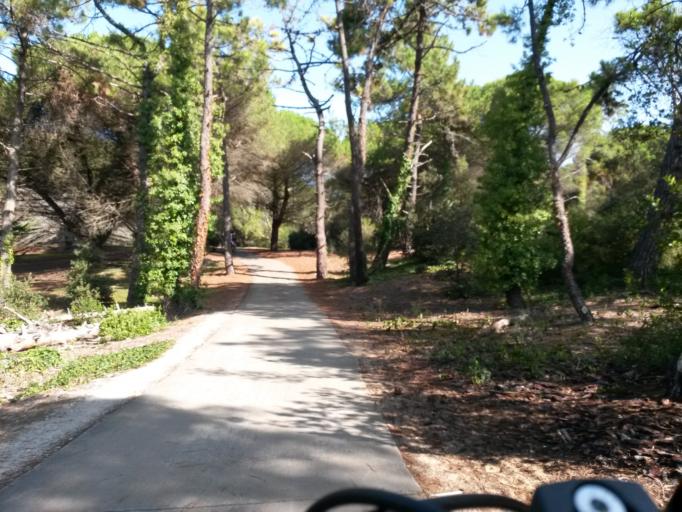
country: FR
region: Poitou-Charentes
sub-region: Departement de la Charente-Maritime
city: Le Bois-Plage-en-Re
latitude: 46.1801
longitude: -1.3759
